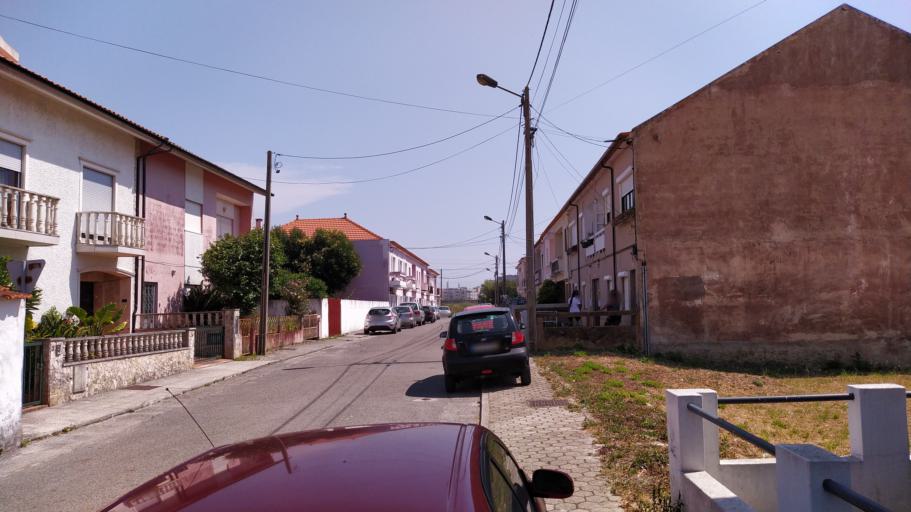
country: PT
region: Aveiro
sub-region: Aveiro
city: Aveiro
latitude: 40.6448
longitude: -8.6370
